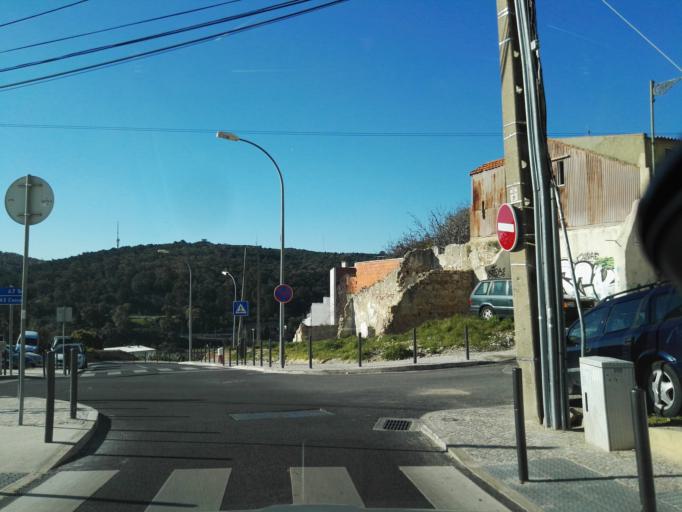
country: PT
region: Lisbon
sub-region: Lisbon
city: Lisbon
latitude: 38.7245
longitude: -9.1669
